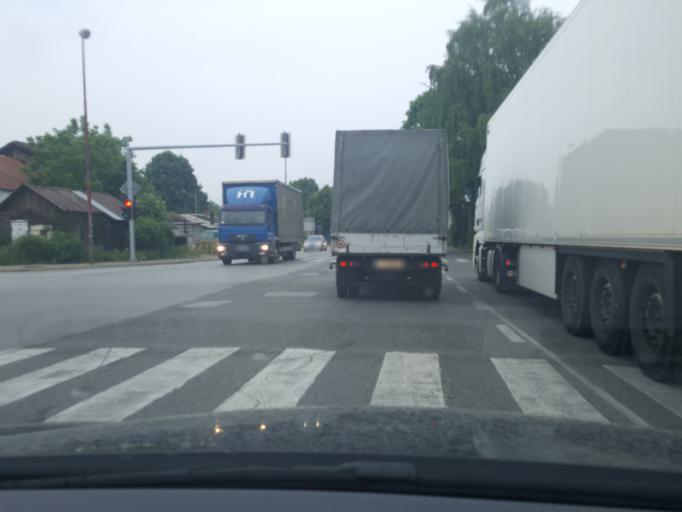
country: RS
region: Central Serbia
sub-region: Kolubarski Okrug
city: Valjevo
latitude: 44.2740
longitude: 19.8835
